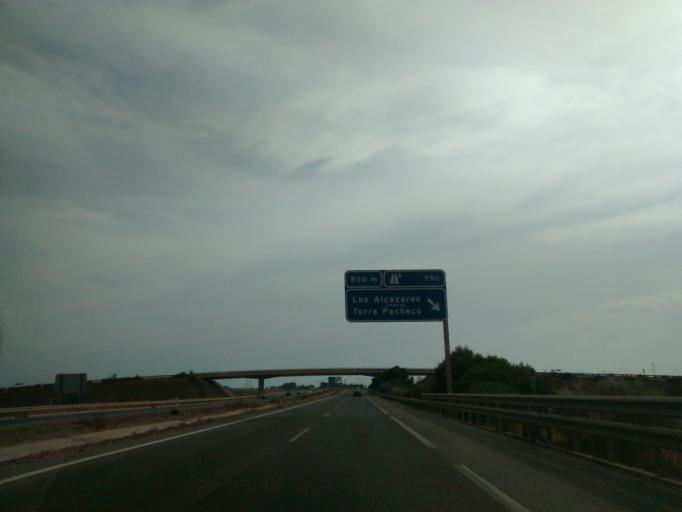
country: ES
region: Murcia
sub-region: Murcia
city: Los Alcazares
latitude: 37.7469
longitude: -0.8672
